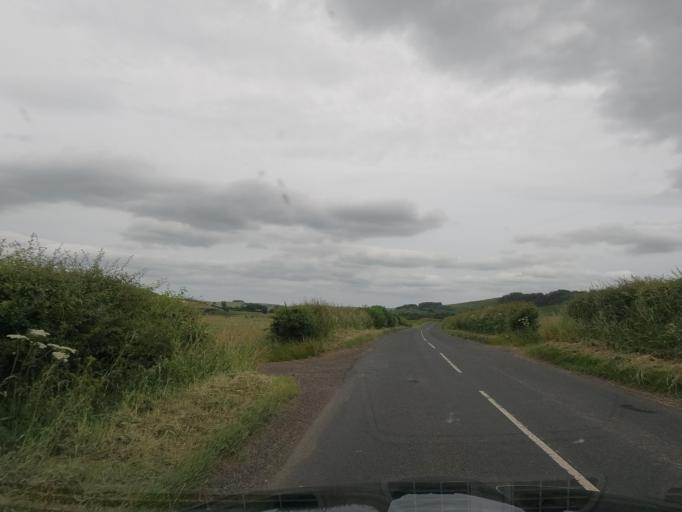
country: GB
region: England
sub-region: Northumberland
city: Doddington
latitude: 55.5545
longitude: -1.9879
